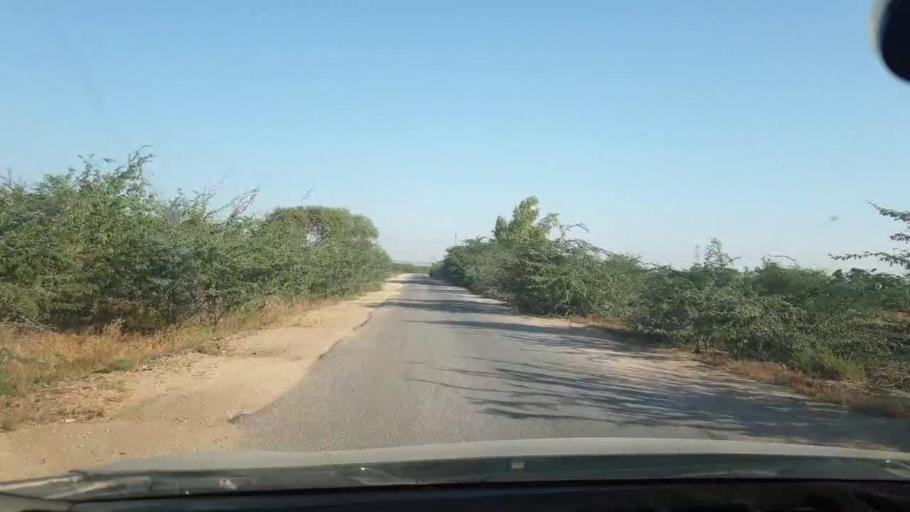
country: PK
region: Sindh
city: Malir Cantonment
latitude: 25.1532
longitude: 67.1905
